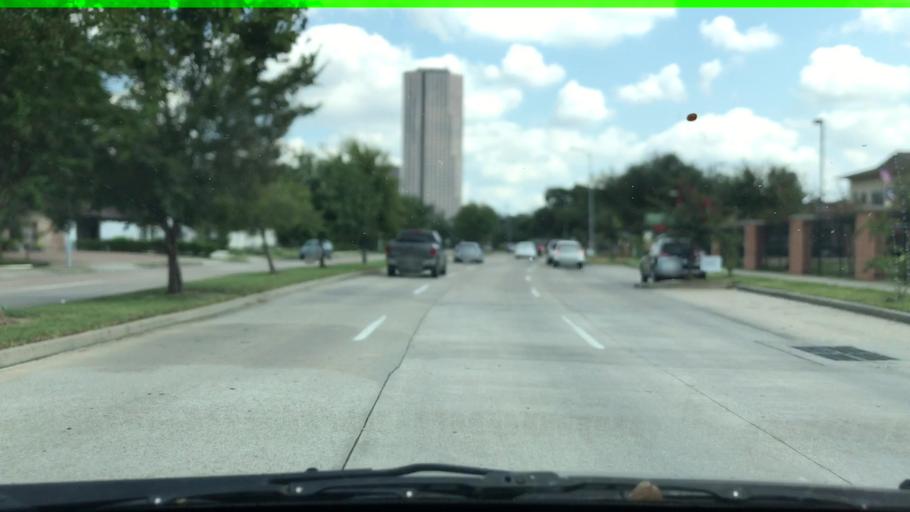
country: US
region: Texas
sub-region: Harris County
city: Hunters Creek Village
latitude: 29.7500
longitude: -95.4918
